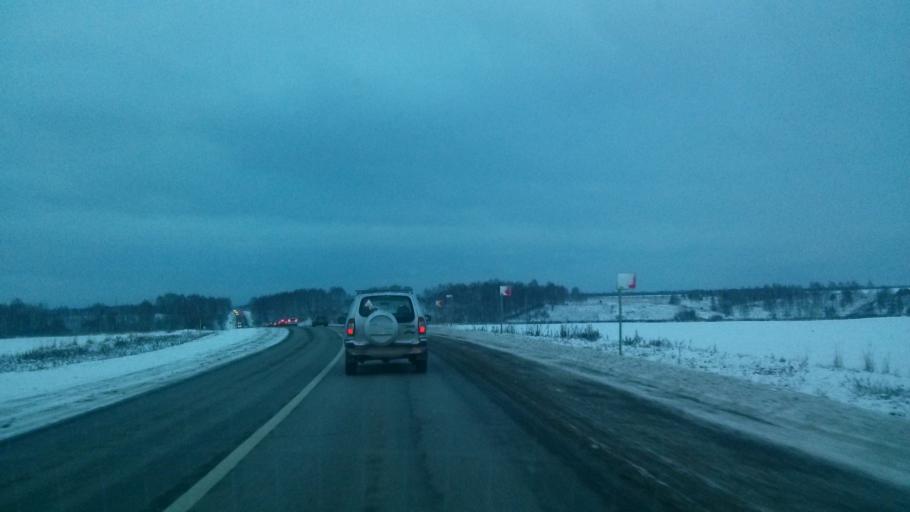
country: RU
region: Nizjnij Novgorod
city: Bogorodsk
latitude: 56.0977
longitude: 43.5827
